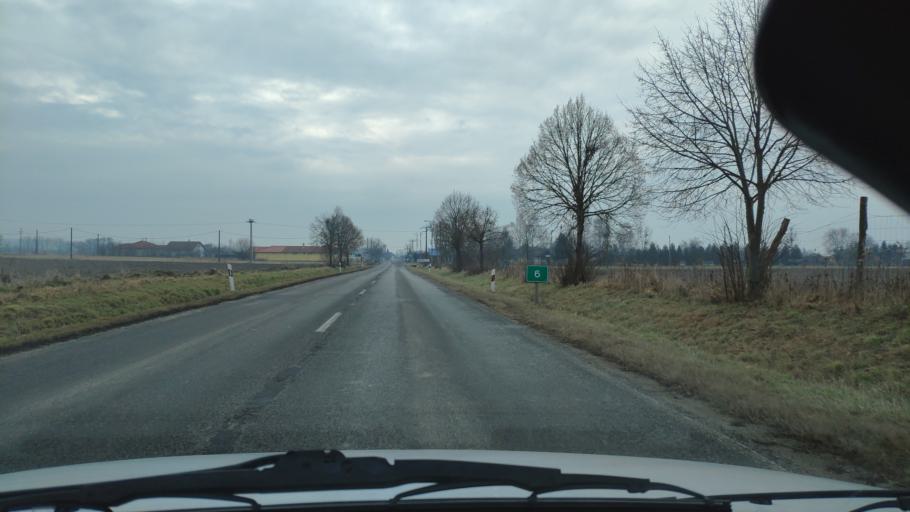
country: HU
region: Zala
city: Nagykanizsa
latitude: 46.5084
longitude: 16.9850
